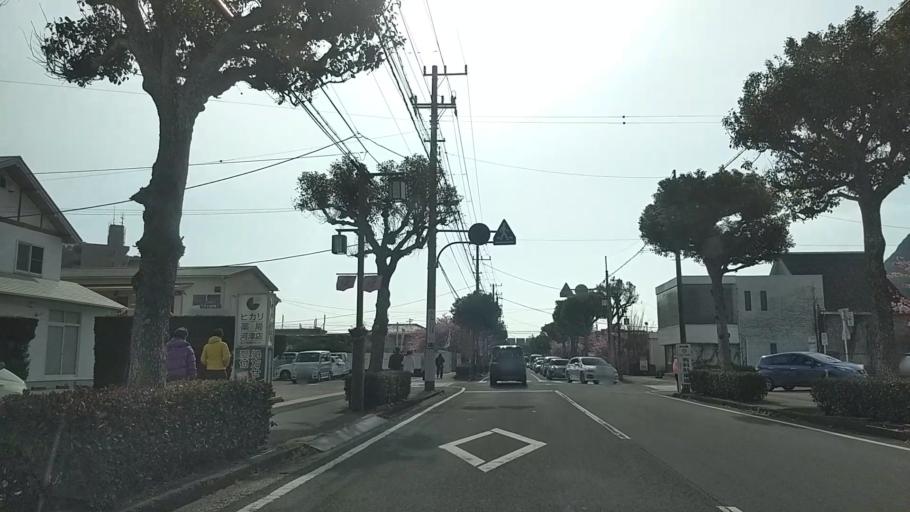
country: JP
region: Shizuoka
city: Shimoda
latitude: 34.7491
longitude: 138.9941
